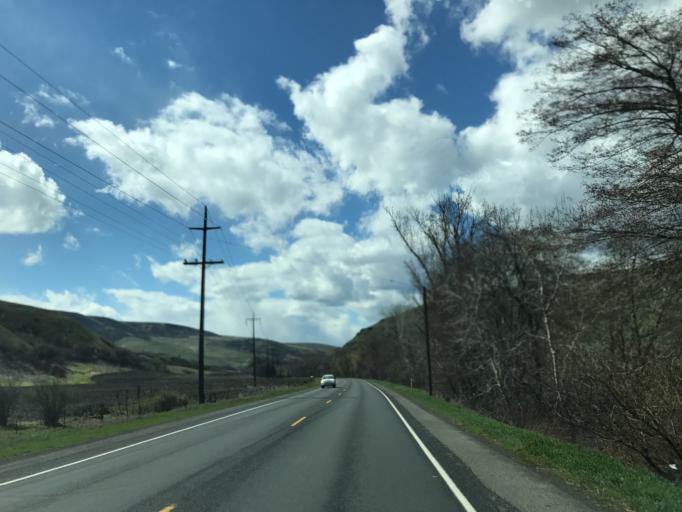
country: US
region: Idaho
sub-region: Nez Perce County
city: Lapwai
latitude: 46.3655
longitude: -116.7434
